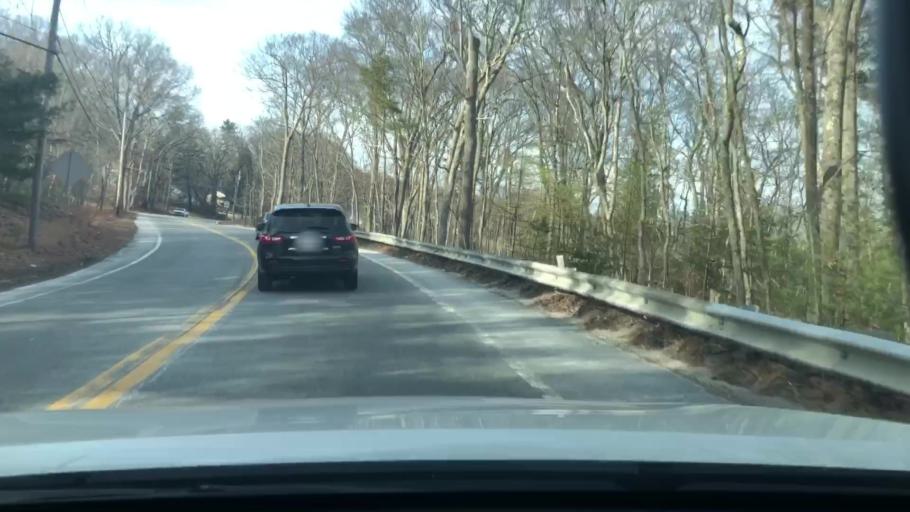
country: US
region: Massachusetts
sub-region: Worcester County
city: Grafton
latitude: 42.2018
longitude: -71.6595
